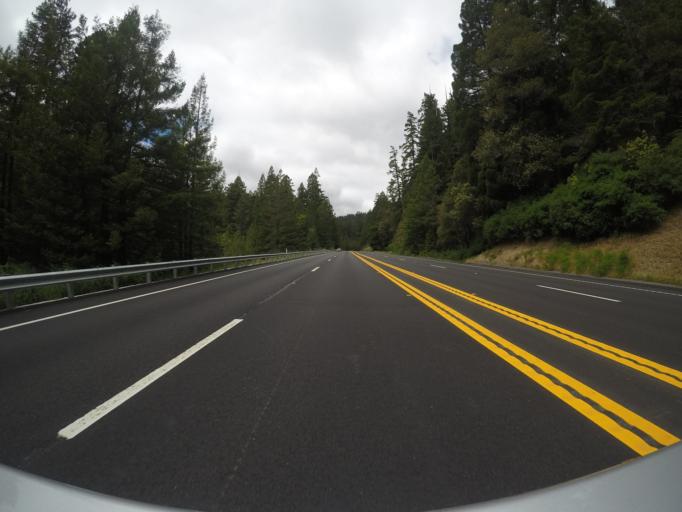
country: US
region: California
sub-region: Humboldt County
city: Rio Dell
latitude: 40.3353
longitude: -123.9310
